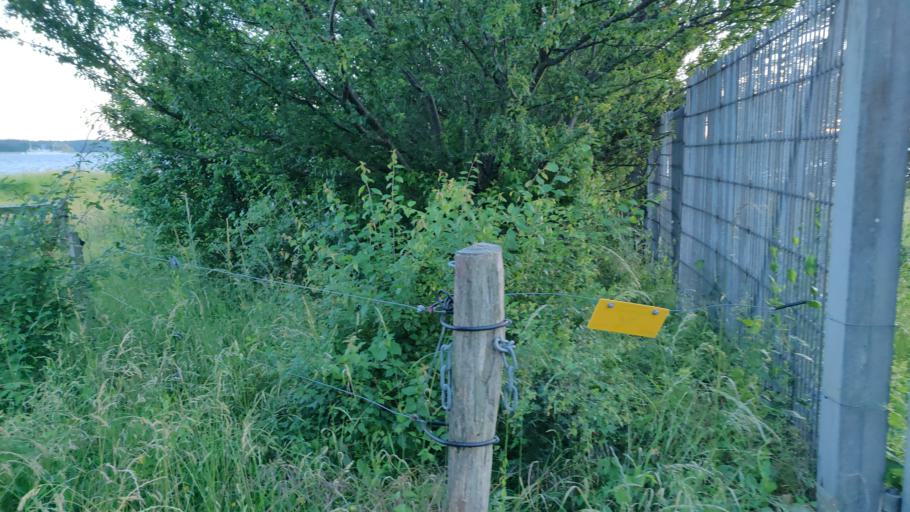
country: DK
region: Zealand
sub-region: Roskilde Kommune
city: Roskilde
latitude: 55.6843
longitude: 12.0761
